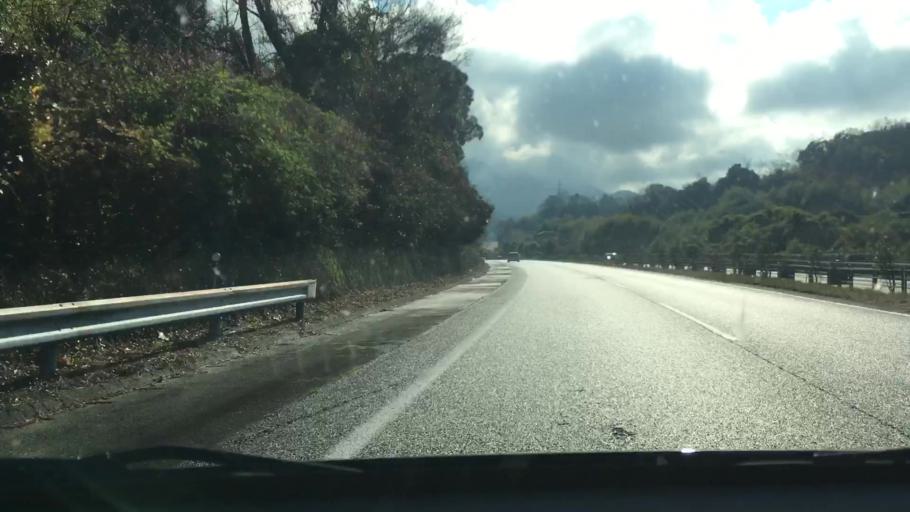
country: JP
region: Kumamoto
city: Matsubase
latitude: 32.5589
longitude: 130.6962
